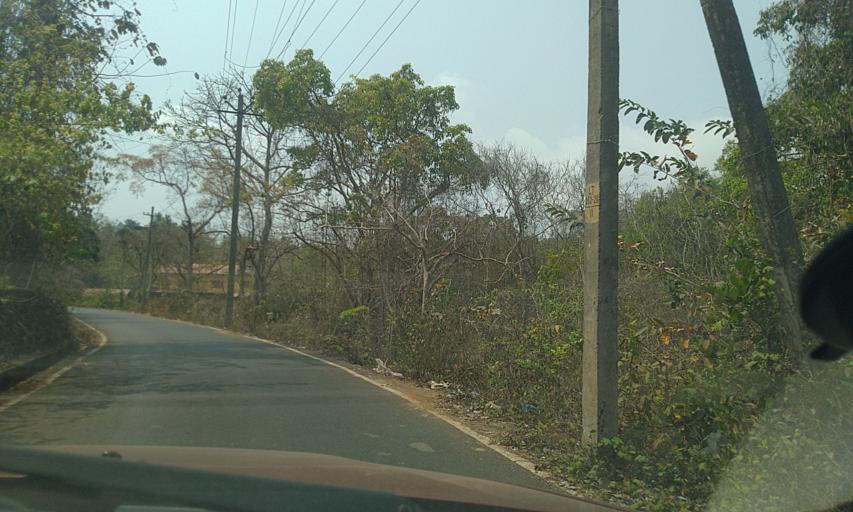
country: IN
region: Goa
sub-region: North Goa
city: Serula
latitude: 15.5243
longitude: 73.8395
